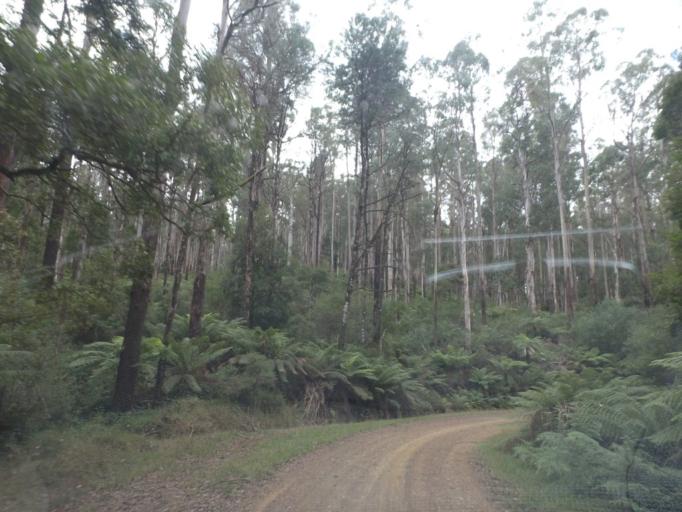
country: AU
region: Victoria
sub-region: Murrindindi
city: Alexandra
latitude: -37.4405
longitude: 145.9618
